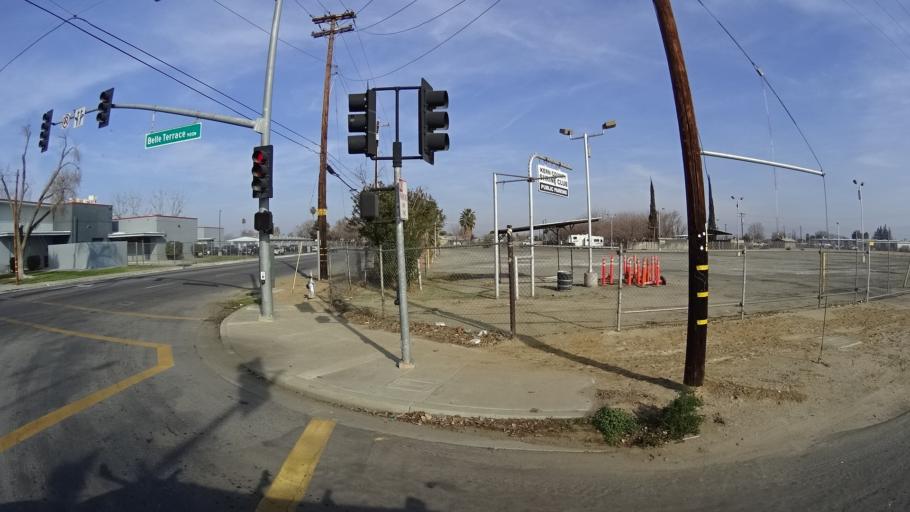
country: US
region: California
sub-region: Kern County
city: Bakersfield
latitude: 35.3466
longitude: -119.0117
